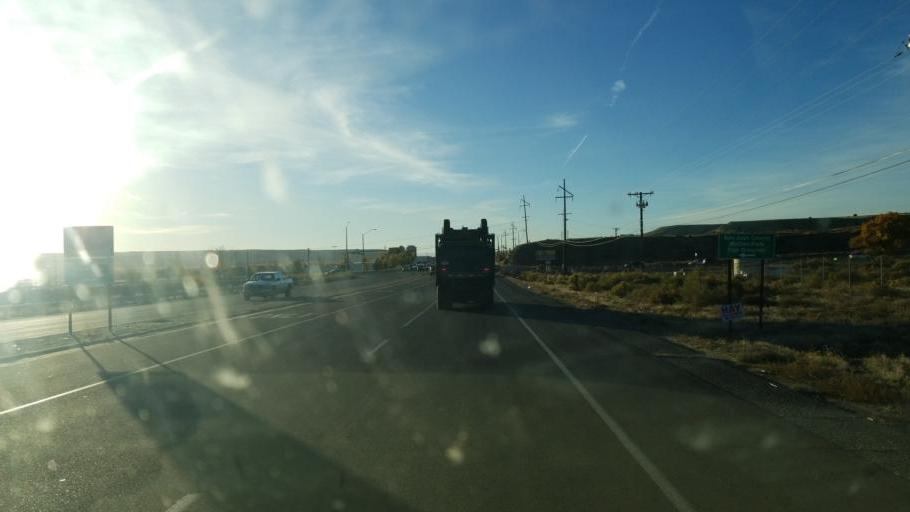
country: US
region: New Mexico
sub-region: San Juan County
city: Lee Acres
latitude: 36.7020
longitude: -108.0927
